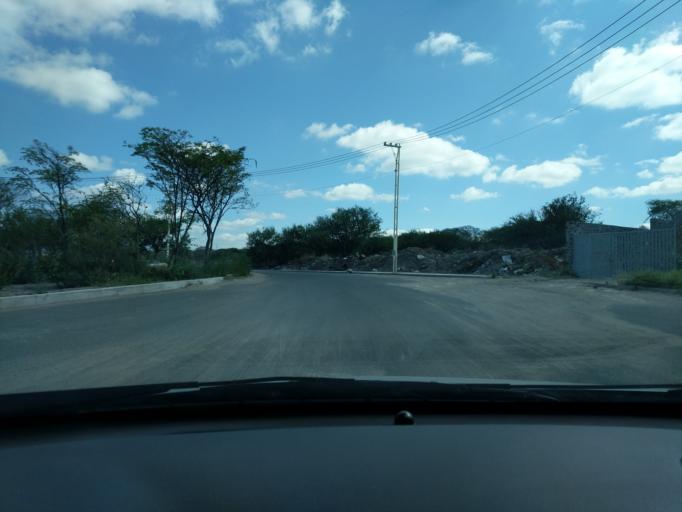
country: MX
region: Queretaro
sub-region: Queretaro
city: Patria Nueva
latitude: 20.6481
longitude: -100.4838
